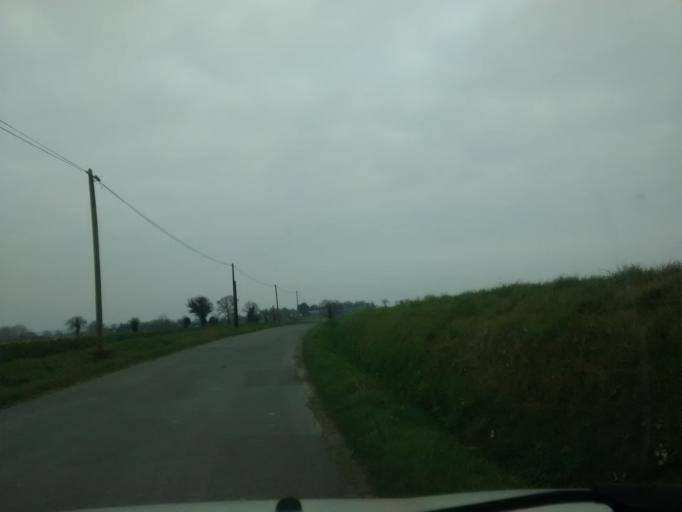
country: FR
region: Brittany
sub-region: Departement d'Ille-et-Vilaine
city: Bazouges-la-Perouse
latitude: 48.4034
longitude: -1.5679
